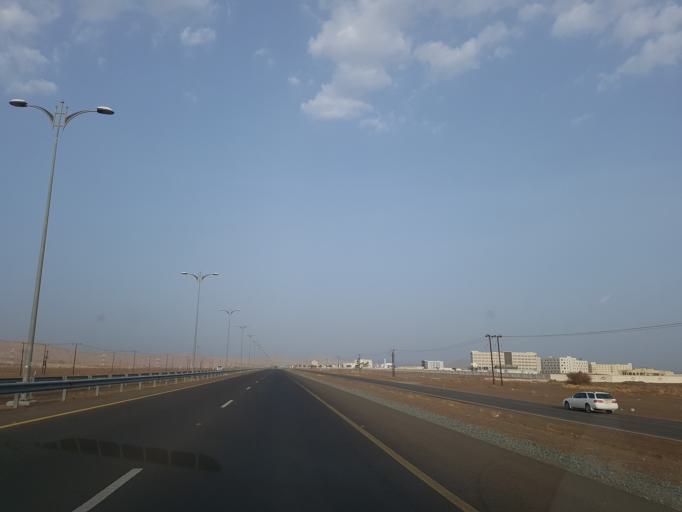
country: OM
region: Al Buraimi
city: Al Buraymi
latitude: 24.2382
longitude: 55.8847
